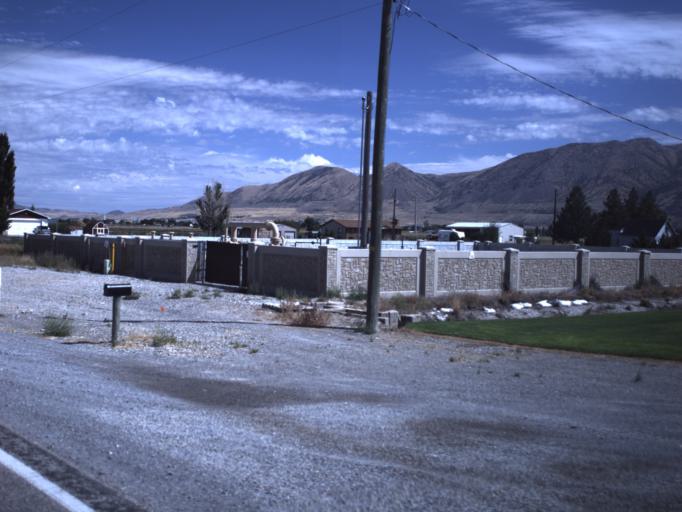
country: US
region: Utah
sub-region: Box Elder County
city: Elwood
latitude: 41.6683
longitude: -112.1408
